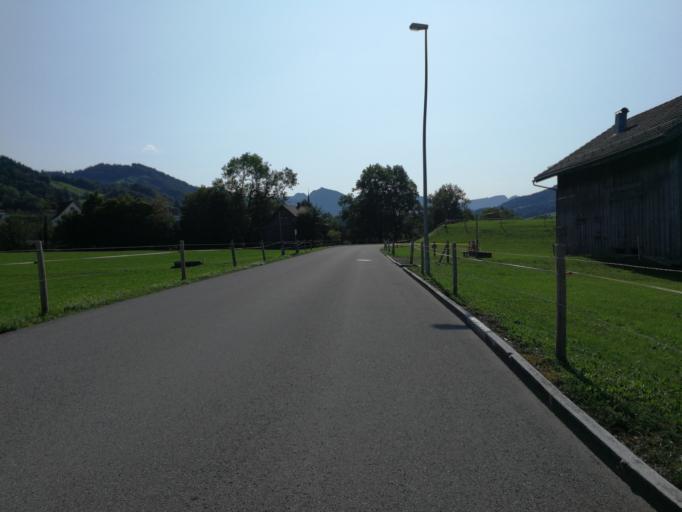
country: CH
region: Saint Gallen
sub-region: Wahlkreis Toggenburg
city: Ebnat-Kappel
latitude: 47.2643
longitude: 9.1168
